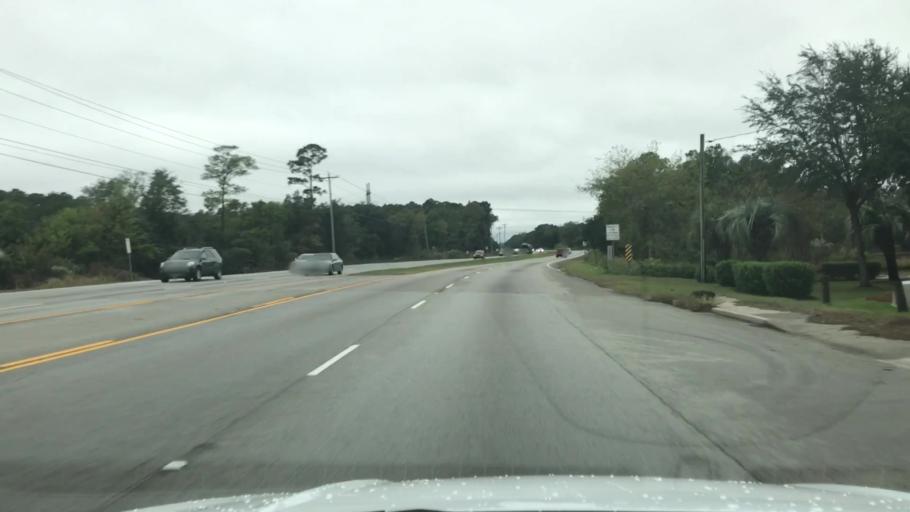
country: US
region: South Carolina
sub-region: Charleston County
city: Shell Point
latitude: 32.7937
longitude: -80.0561
